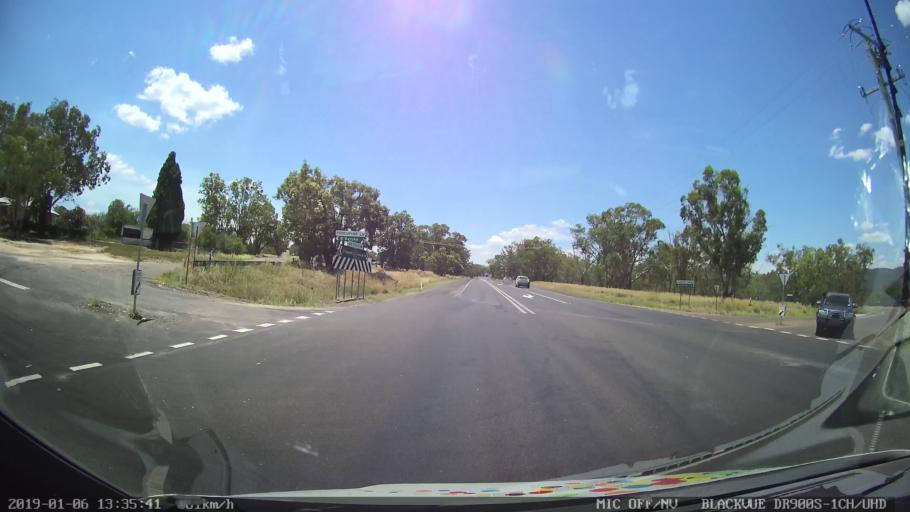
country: AU
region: New South Wales
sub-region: Tamworth Municipality
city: Kootingal
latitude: -31.0746
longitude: 151.0274
